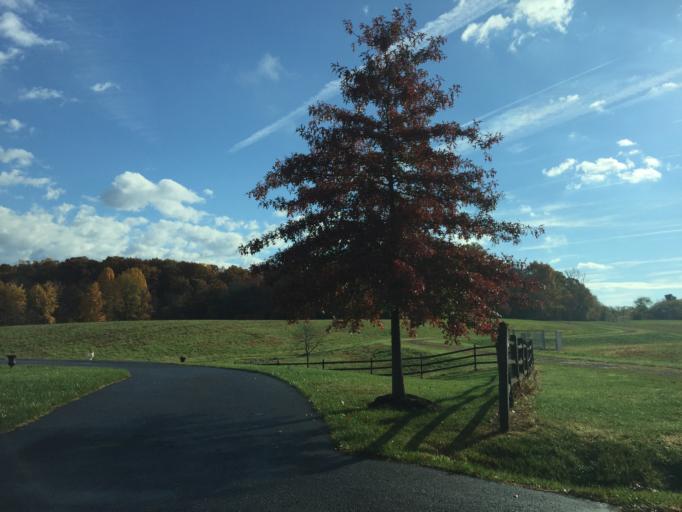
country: US
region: Maryland
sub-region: Howard County
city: Highland
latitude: 39.2720
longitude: -77.0037
